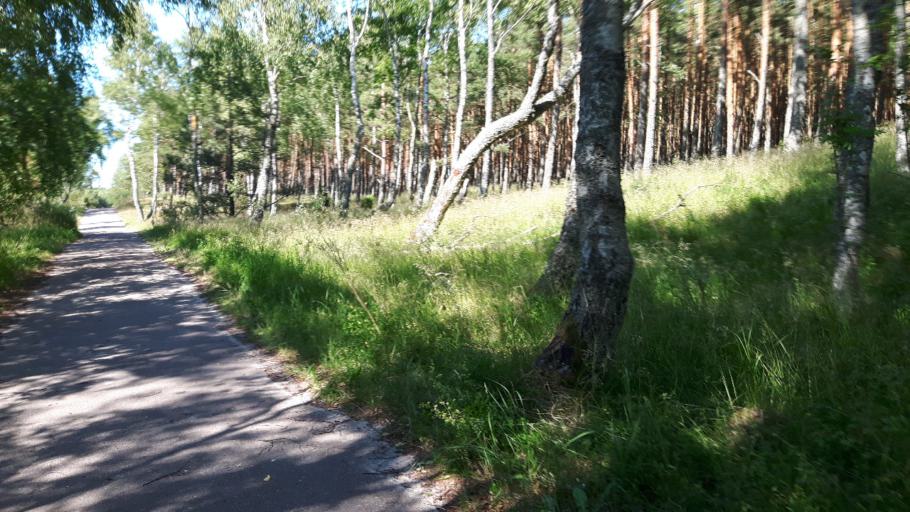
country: LT
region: Klaipedos apskritis
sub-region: Klaipeda
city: Klaipeda
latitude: 55.6891
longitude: 21.1034
